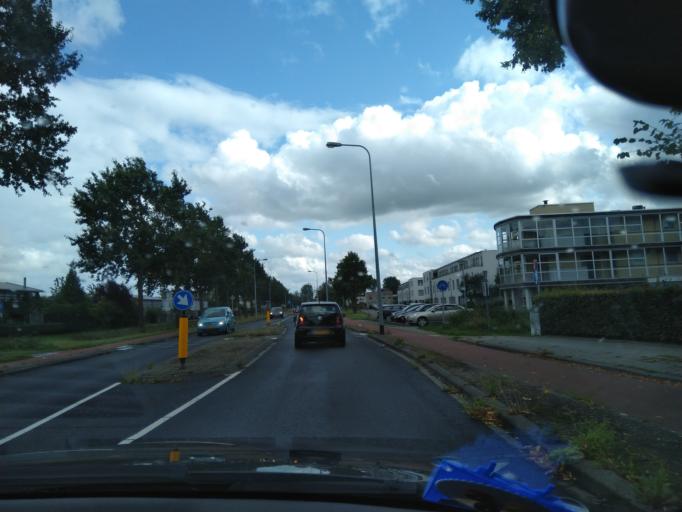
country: NL
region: Groningen
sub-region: Gemeente Groningen
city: Groningen
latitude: 53.2044
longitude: 6.5090
